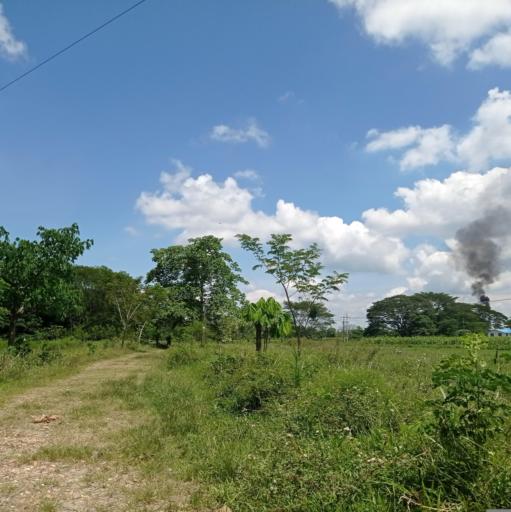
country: CO
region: Santander
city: Barrancabermeja
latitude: 7.0935
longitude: -73.8761
